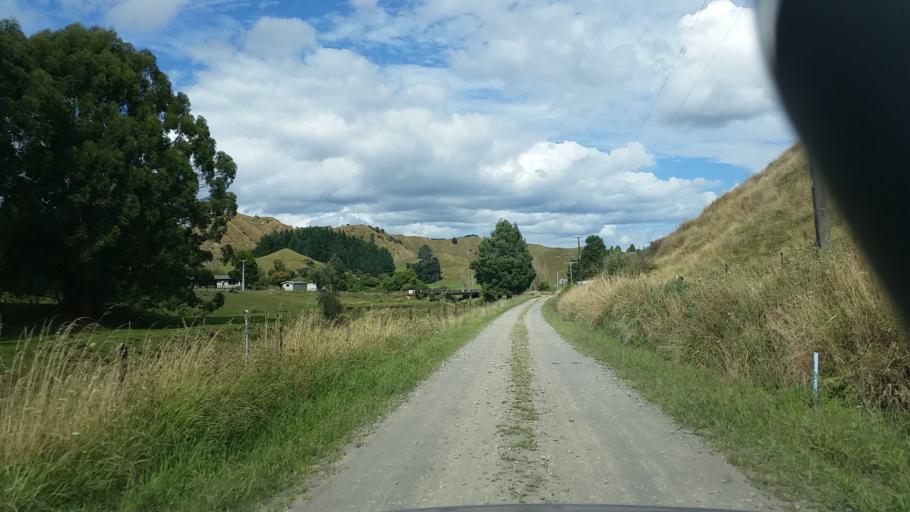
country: NZ
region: Taranaki
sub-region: South Taranaki District
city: Eltham
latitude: -39.2600
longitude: 174.5661
